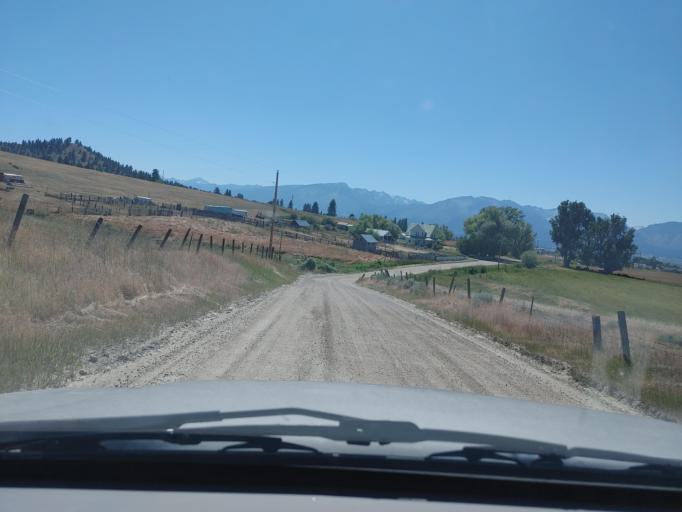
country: US
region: Montana
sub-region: Ravalli County
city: Hamilton
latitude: 46.2770
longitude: -114.0263
